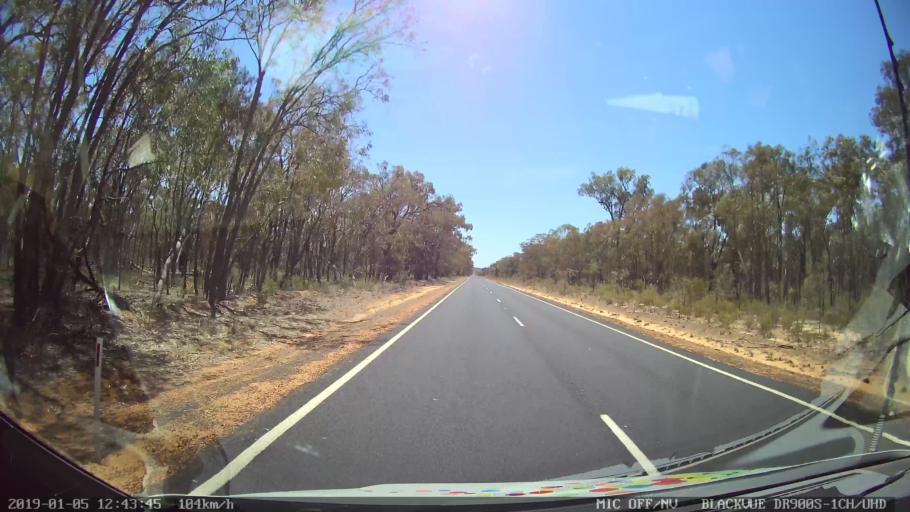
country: AU
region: New South Wales
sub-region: Warrumbungle Shire
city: Coonabarabran
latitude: -31.1447
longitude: 149.5283
